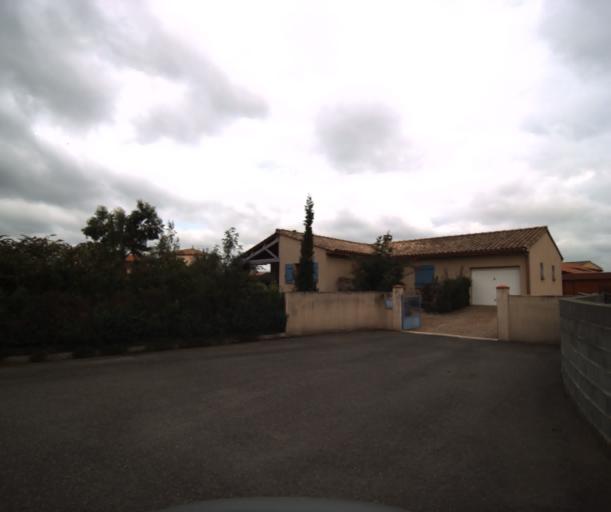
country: FR
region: Midi-Pyrenees
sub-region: Departement de la Haute-Garonne
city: Le Fauga
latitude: 43.4436
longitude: 1.2914
